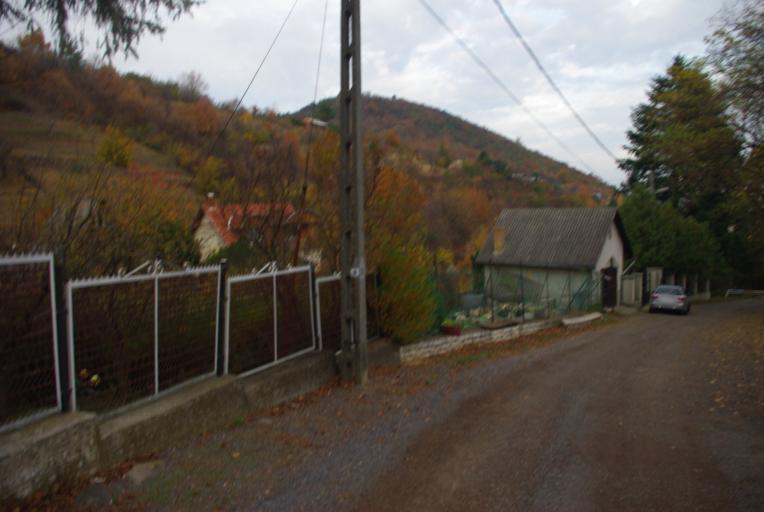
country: HU
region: Borsod-Abauj-Zemplen
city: Satoraljaujhely
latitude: 48.3908
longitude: 21.6328
